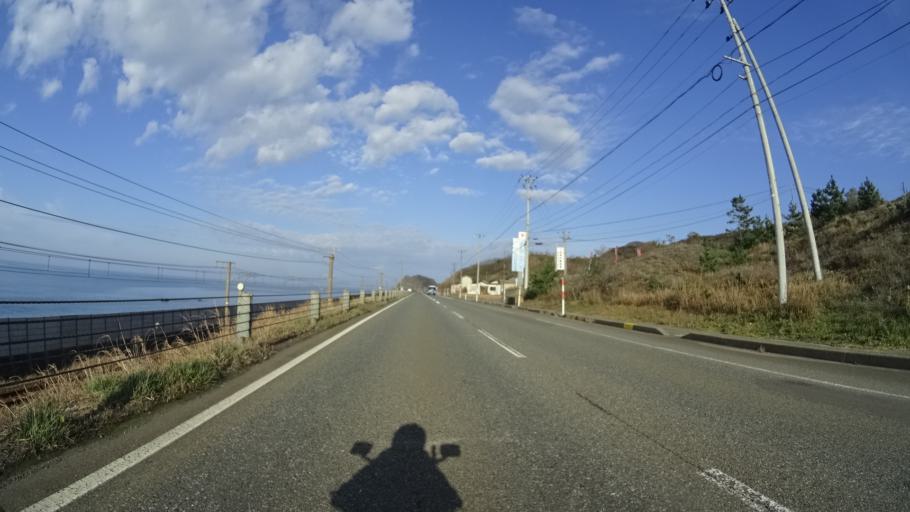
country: JP
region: Niigata
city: Kashiwazaki
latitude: 37.3085
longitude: 138.4213
